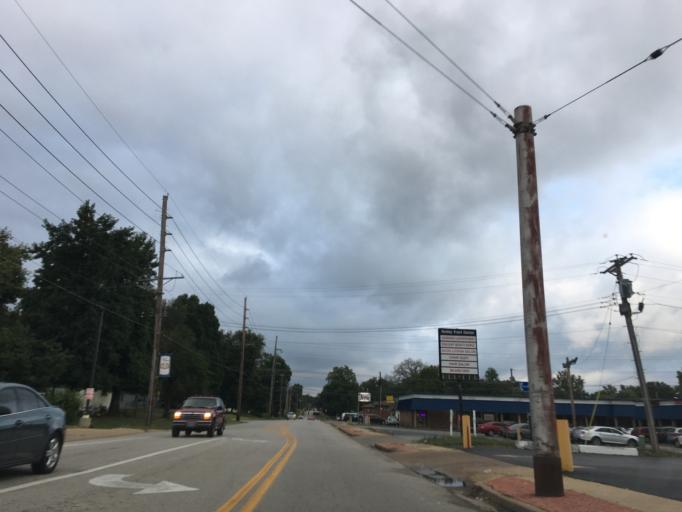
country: US
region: Missouri
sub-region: Saint Louis County
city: Berkeley
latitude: 38.7626
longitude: -90.3367
